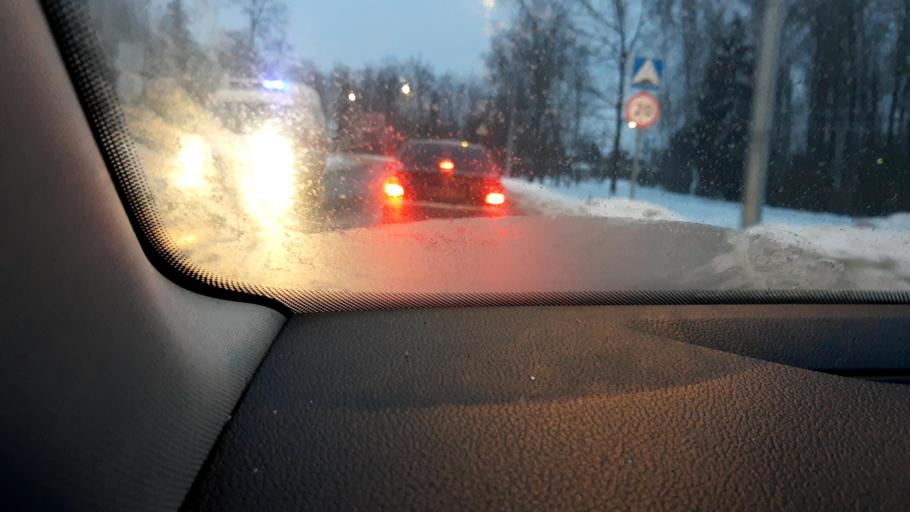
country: RU
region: Moskovskaya
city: Troitsk
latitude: 55.3057
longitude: 37.1870
